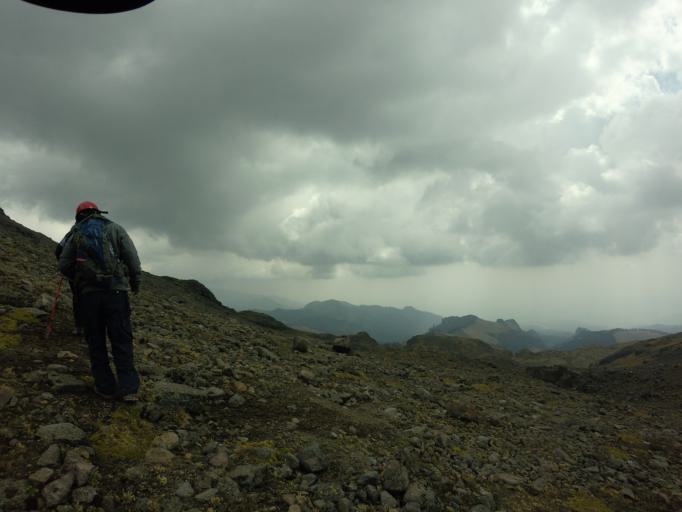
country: MX
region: Mexico
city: Amecameca de Juarez
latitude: 19.1556
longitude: -98.6417
